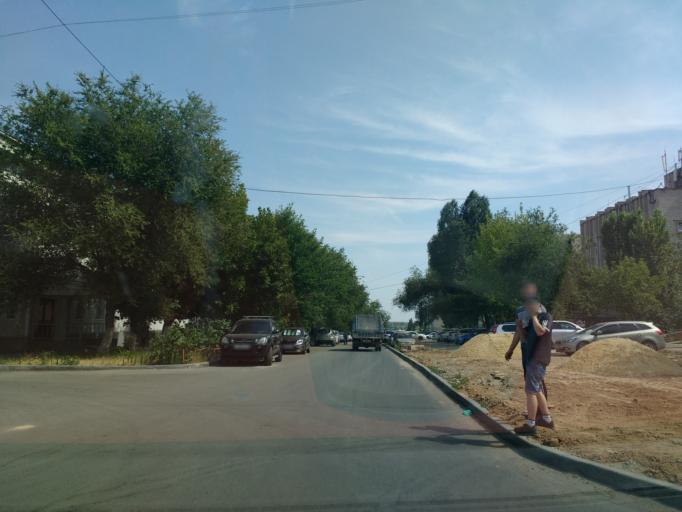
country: RU
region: Volgograd
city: Volgograd
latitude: 48.6912
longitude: 44.4950
